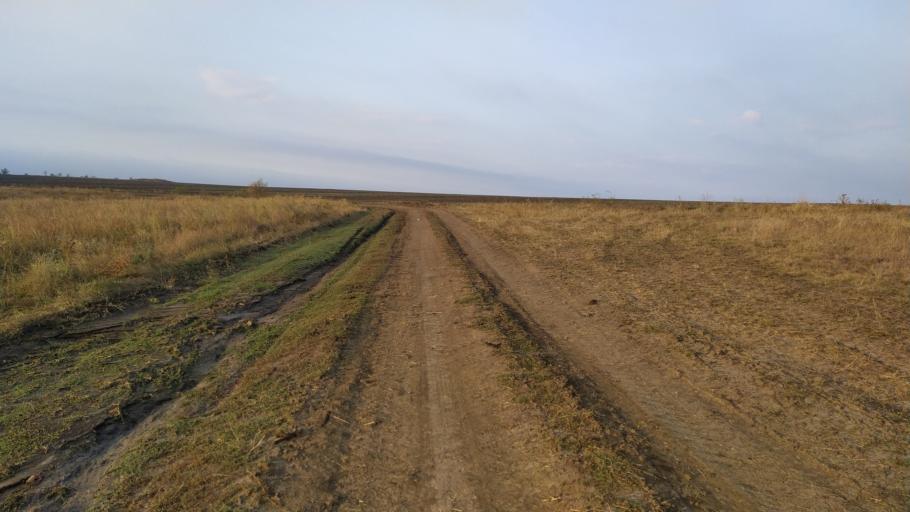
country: RU
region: Rostov
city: Gornyy
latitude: 47.8918
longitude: 40.2411
